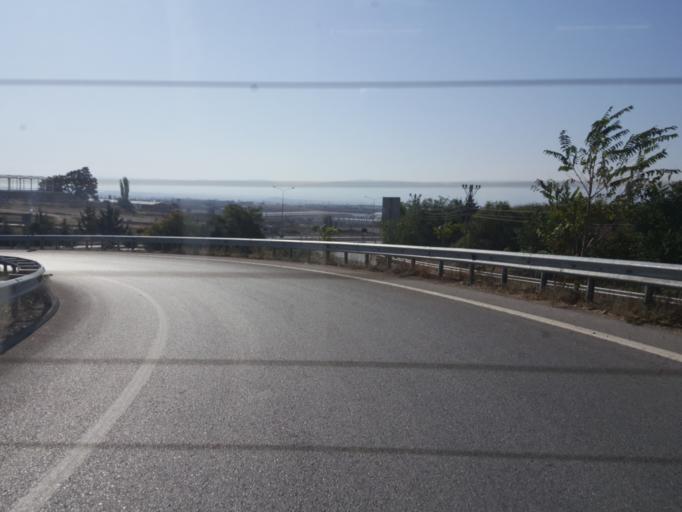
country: TR
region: Amasya
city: Merzifon
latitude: 40.8567
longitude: 35.4615
